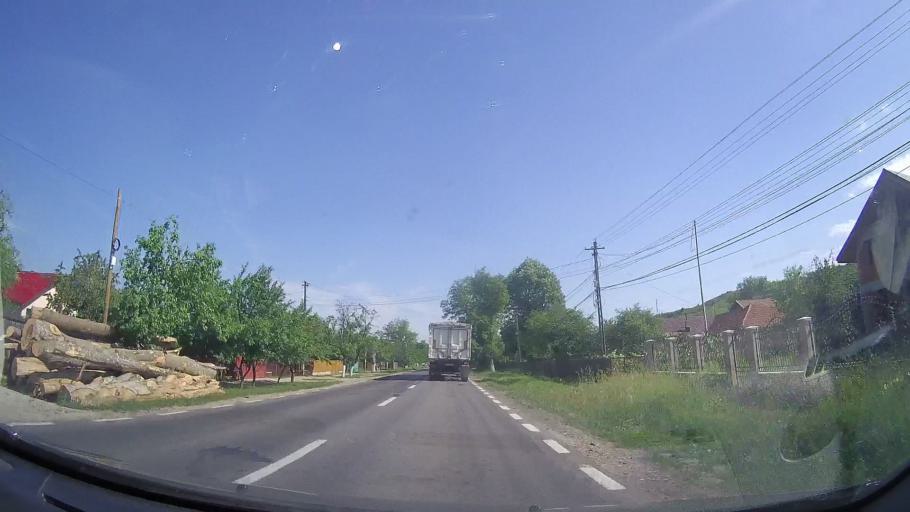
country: RO
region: Prahova
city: Drajna de Jos
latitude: 45.2163
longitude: 26.0365
